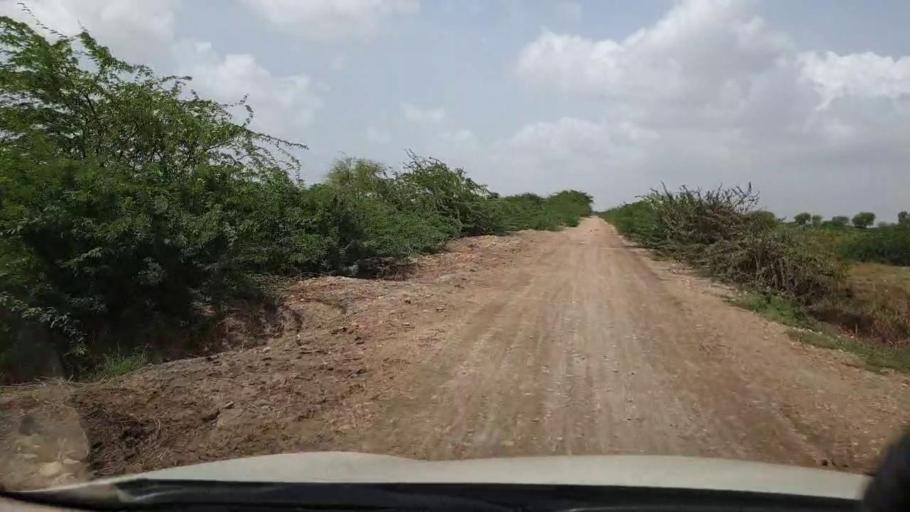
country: PK
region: Sindh
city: Kadhan
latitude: 24.3691
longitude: 68.8522
